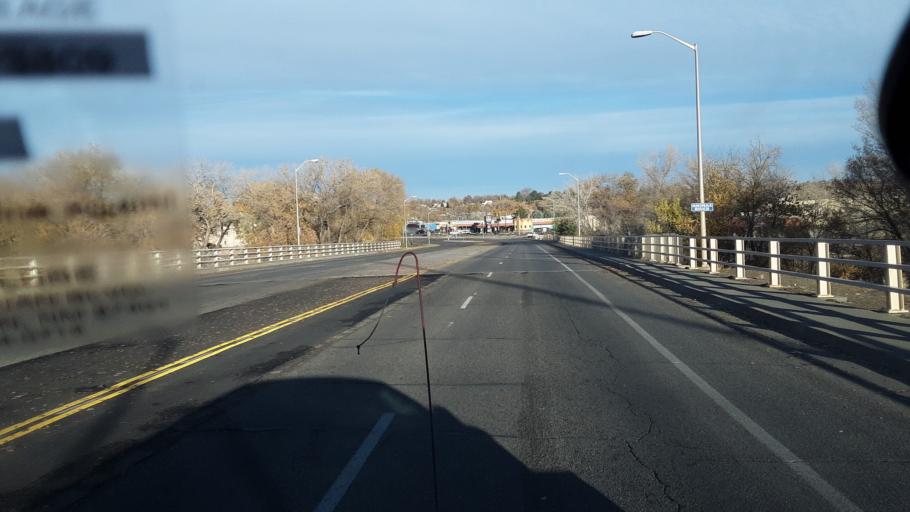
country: US
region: New Mexico
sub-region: San Juan County
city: Farmington
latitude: 36.7266
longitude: -108.1902
